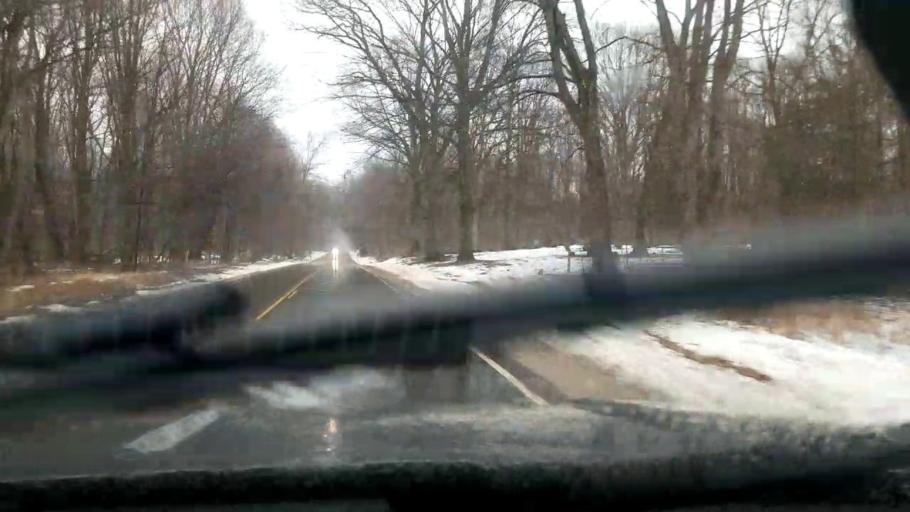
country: US
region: Michigan
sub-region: Jackson County
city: Grass Lake
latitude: 42.3212
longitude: -84.2499
